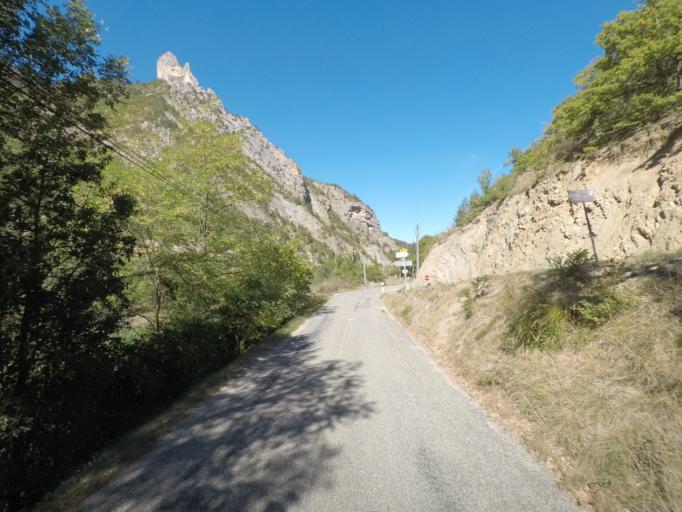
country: FR
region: Rhone-Alpes
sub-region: Departement de la Drome
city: Die
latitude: 44.6477
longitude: 5.2894
